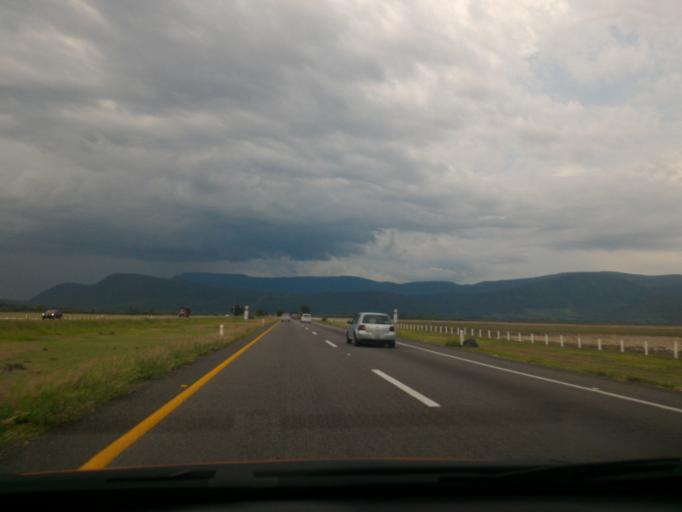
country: MX
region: Jalisco
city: Zacoalco de Torres
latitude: 20.1392
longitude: -103.5054
